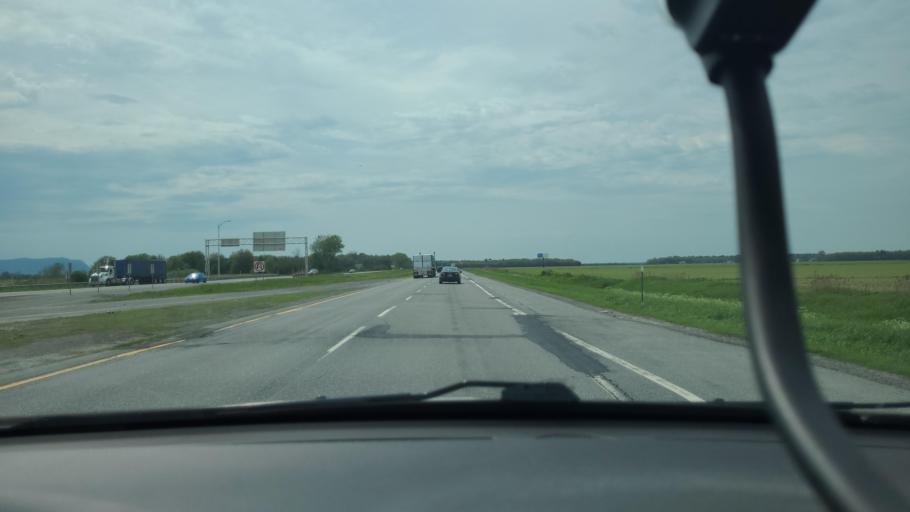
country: CA
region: Quebec
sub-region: Monteregie
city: Saint-Hyacinthe
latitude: 45.6336
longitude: -73.0048
